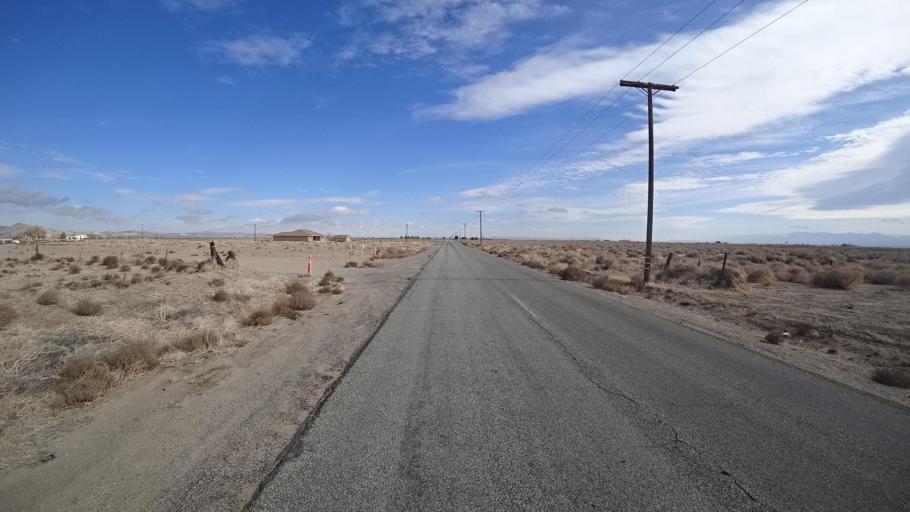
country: US
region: California
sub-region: Kern County
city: Rosamond
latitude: 34.8201
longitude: -118.2291
